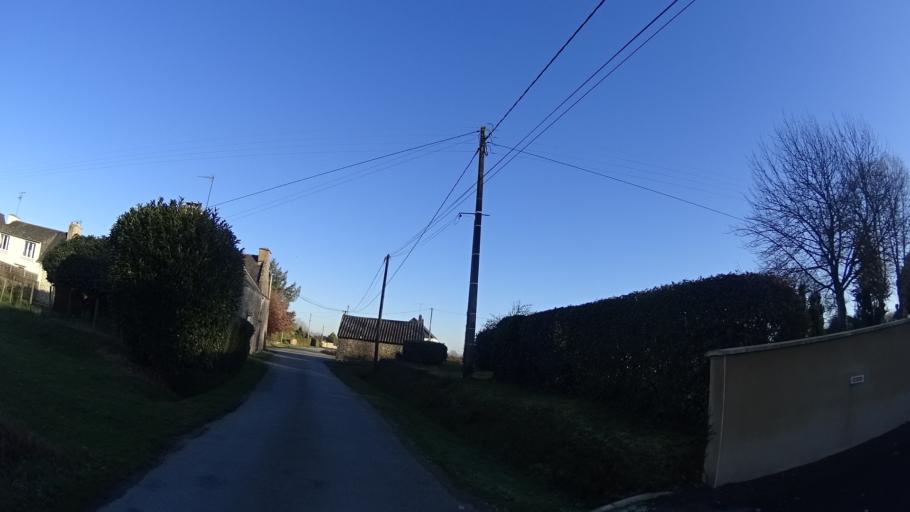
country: FR
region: Brittany
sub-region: Departement du Morbihan
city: Allaire
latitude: 47.6513
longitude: -2.1601
